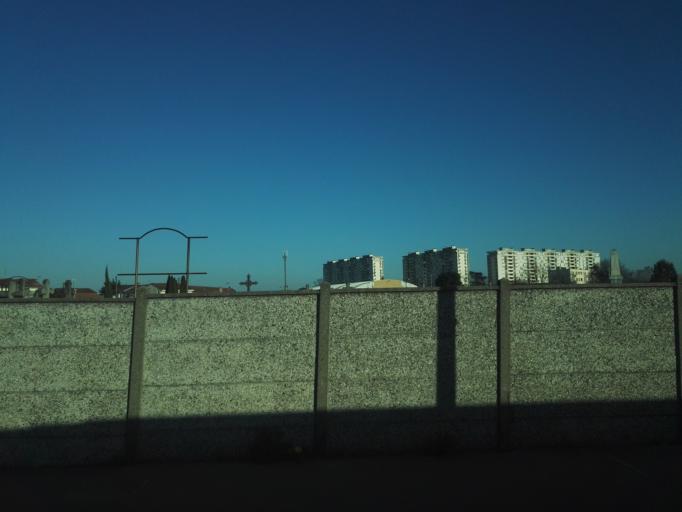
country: FR
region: Aquitaine
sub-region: Departement de la Gironde
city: Talence
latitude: 44.8133
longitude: -0.5822
